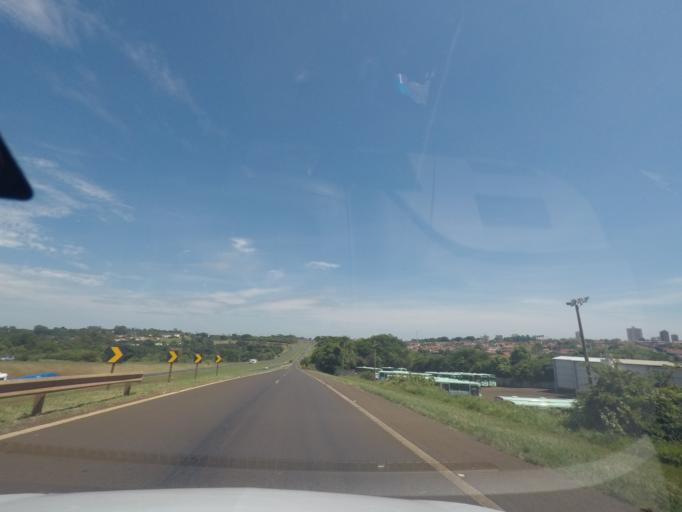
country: BR
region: Sao Paulo
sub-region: Araraquara
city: Araraquara
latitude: -21.8168
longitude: -48.1800
